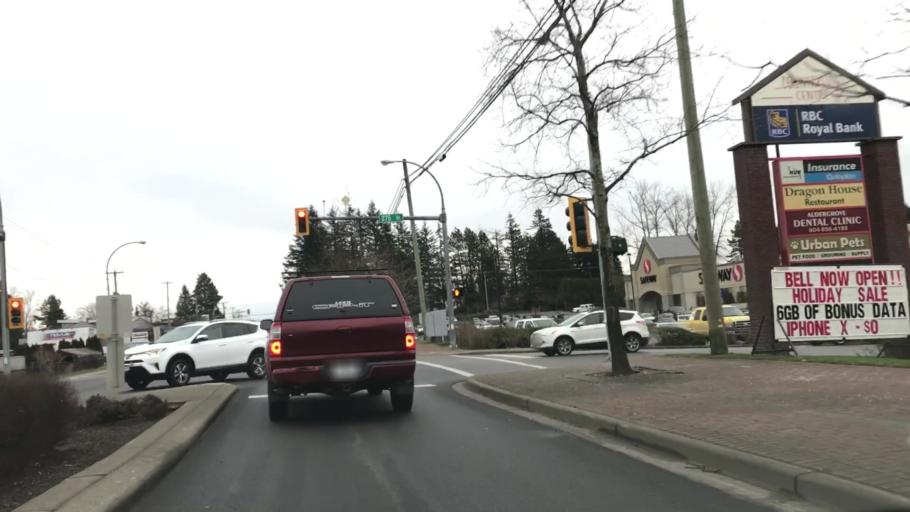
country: CA
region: British Columbia
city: Aldergrove
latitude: 49.0577
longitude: -122.4627
